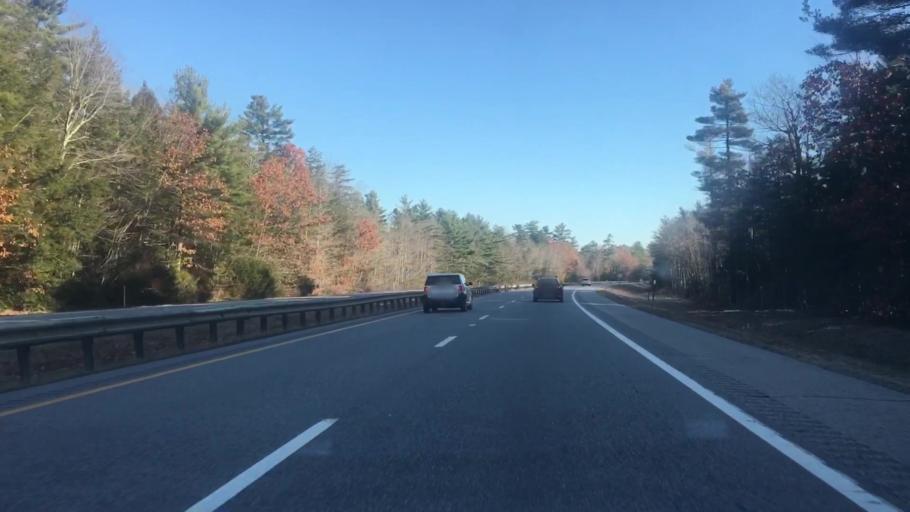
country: US
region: Maine
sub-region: Cumberland County
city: New Gloucester
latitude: 43.9696
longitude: -70.3236
